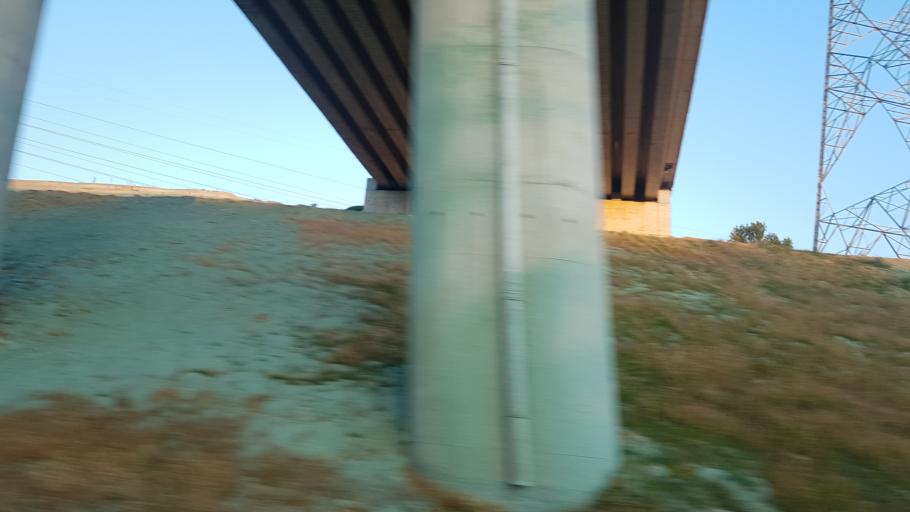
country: TR
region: Kocaeli
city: Tavsanli
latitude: 40.8062
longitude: 29.5199
